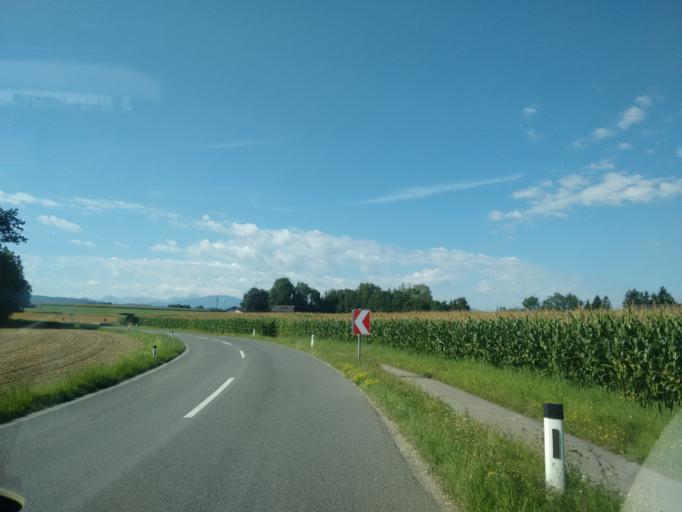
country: AT
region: Upper Austria
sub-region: Politischer Bezirk Steyr-Land
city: Pfarrkirchen bei Bad Hall
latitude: 48.0206
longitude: 14.1888
